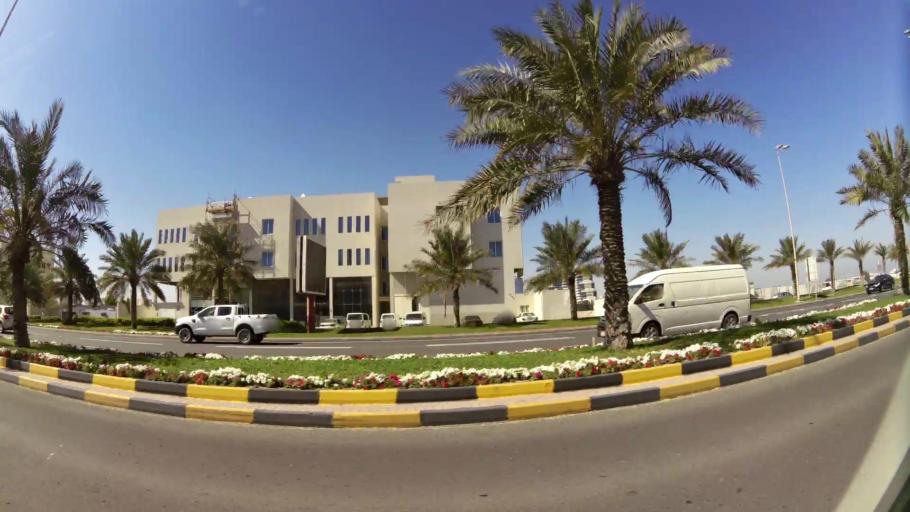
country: BH
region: Muharraq
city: Al Muharraq
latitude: 26.2477
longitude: 50.6074
